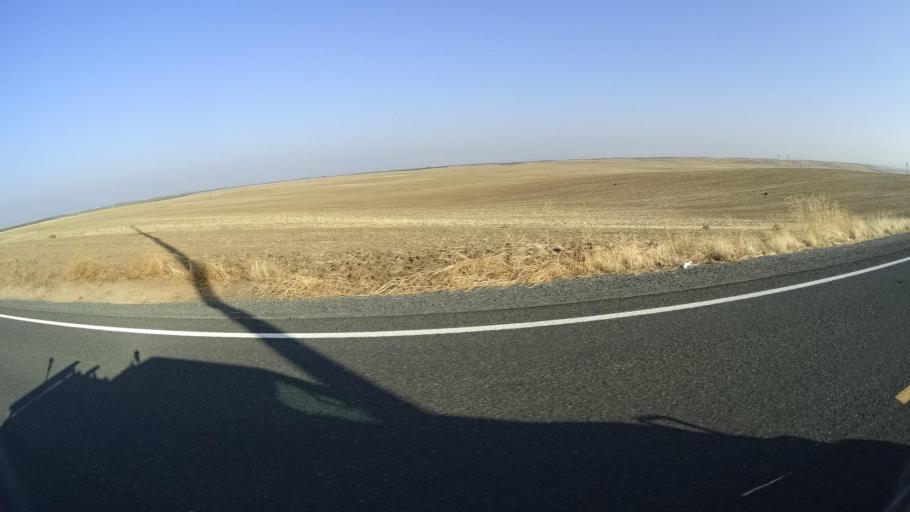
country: US
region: California
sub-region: Tulare County
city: Richgrove
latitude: 35.7620
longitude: -119.0697
